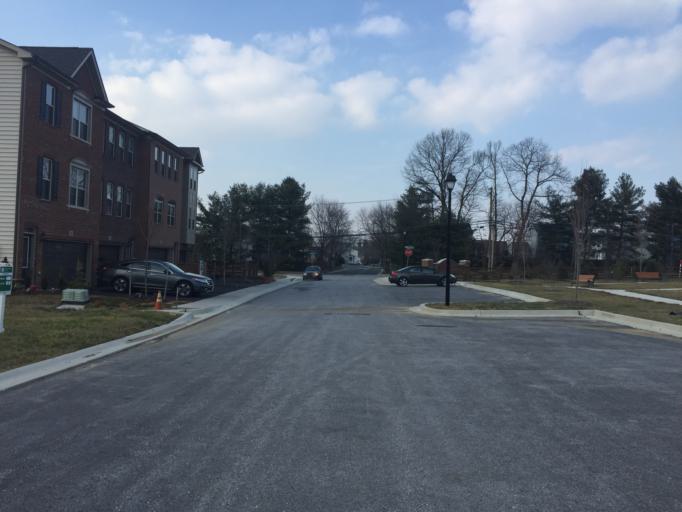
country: US
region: Maryland
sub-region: Anne Arundel County
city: South Gate
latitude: 39.1111
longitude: -76.6289
